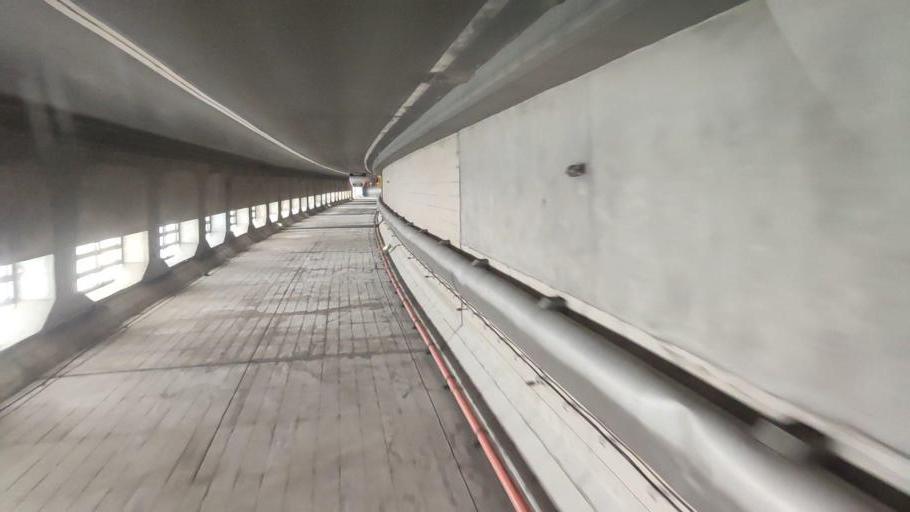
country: JP
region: Hokkaido
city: Rumoi
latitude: 43.7998
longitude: 141.3799
